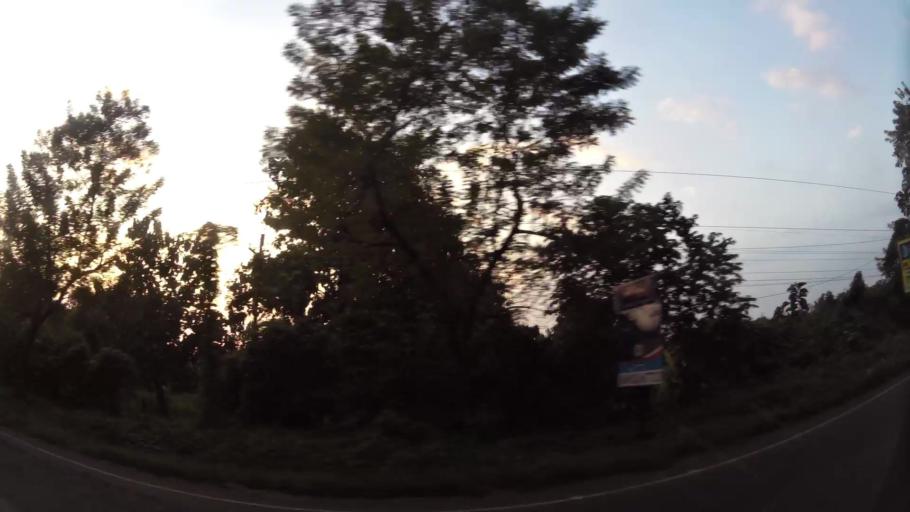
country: GT
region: Retalhuleu
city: Santa Cruz Mulua
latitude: 14.5775
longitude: -91.6291
